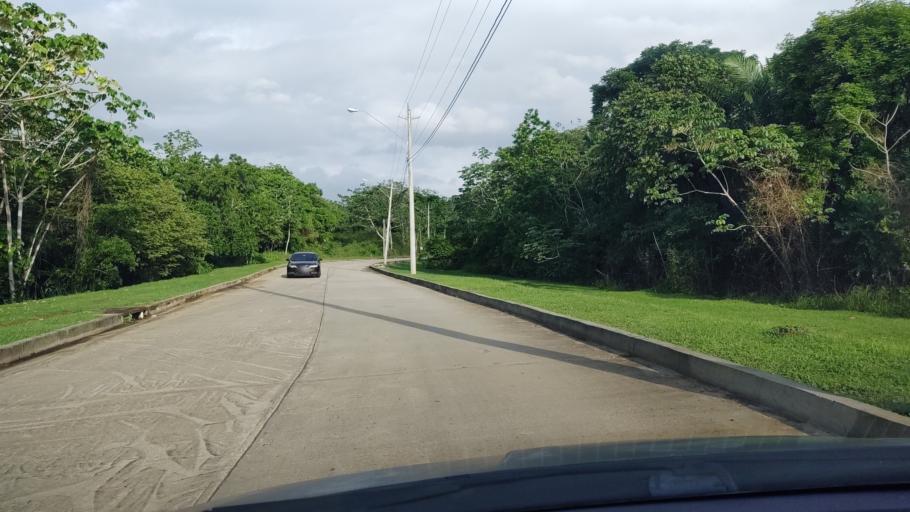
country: PA
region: Panama
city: Nuevo Arraijan
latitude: 8.9251
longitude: -79.7537
